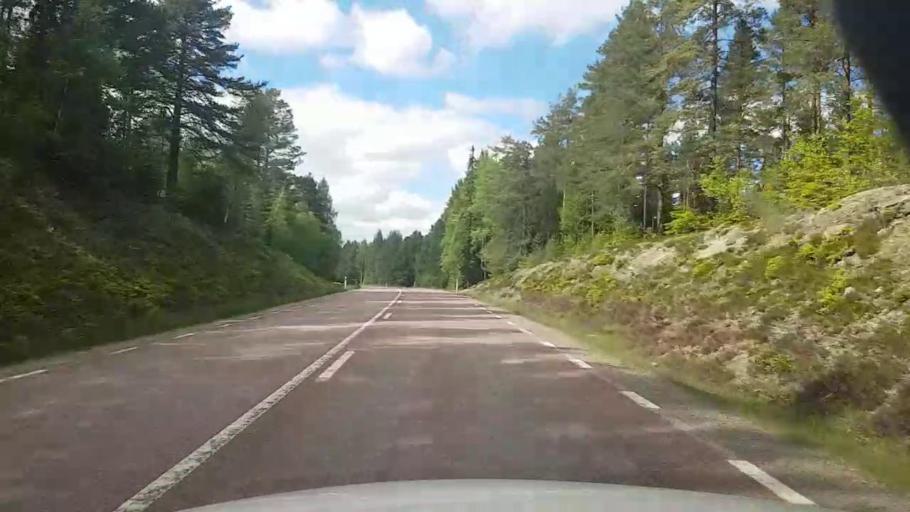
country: SE
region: Gaevleborg
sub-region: Ljusdals Kommun
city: Ljusdal
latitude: 61.7922
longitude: 16.1295
